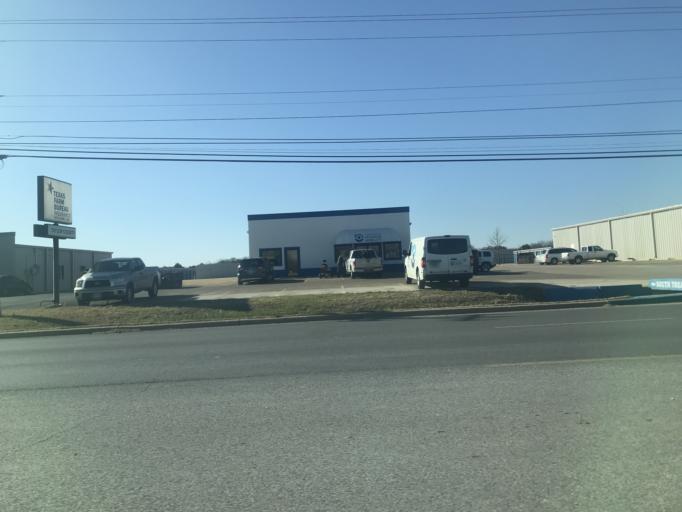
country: US
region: Texas
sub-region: Taylor County
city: Abilene
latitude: 32.4104
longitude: -99.7424
